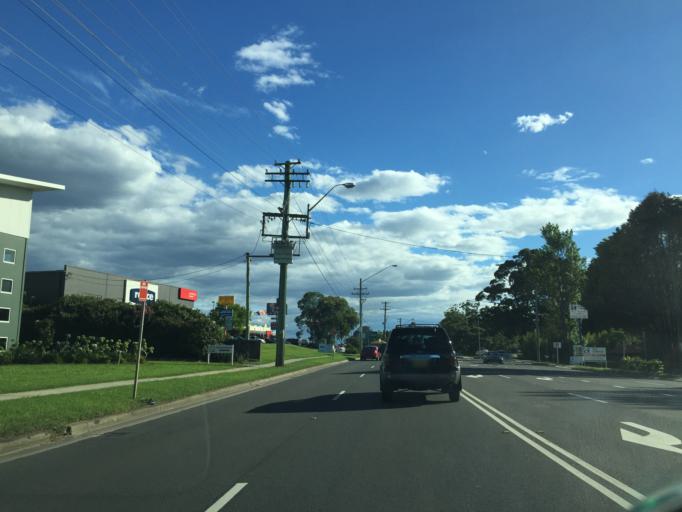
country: AU
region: New South Wales
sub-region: The Hills Shire
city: Glenhaven
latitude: -33.6943
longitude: 151.0317
